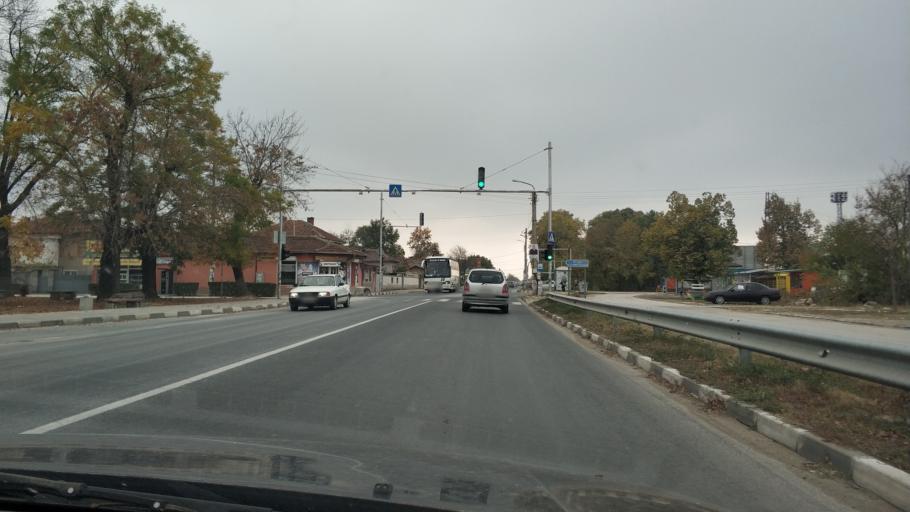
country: BG
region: Plovdiv
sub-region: Obshtina Plovdiv
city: Plovdiv
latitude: 42.2314
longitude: 24.7243
